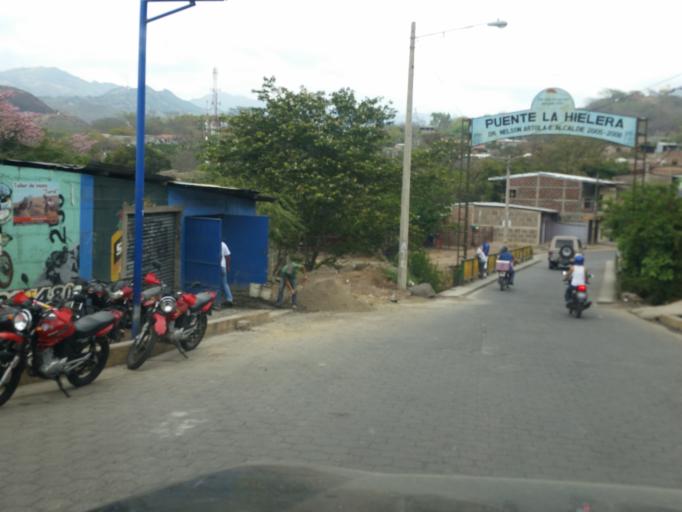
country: NI
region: Matagalpa
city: Matagalpa
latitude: 12.9357
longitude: -85.9105
